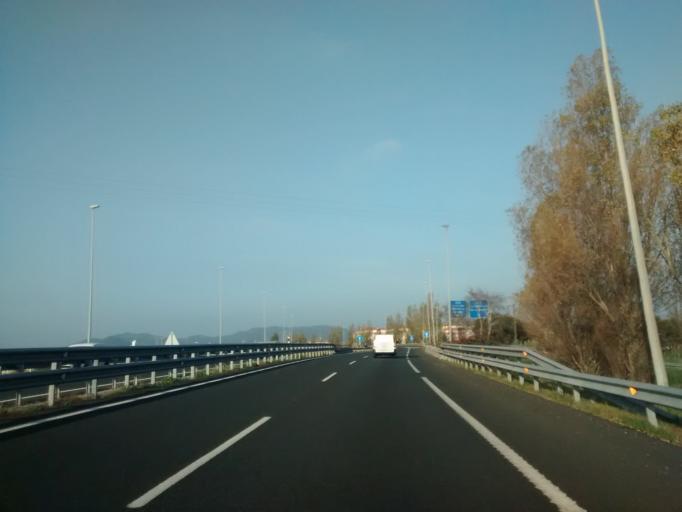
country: ES
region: Cantabria
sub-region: Provincia de Cantabria
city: Santa Cruz de Bezana
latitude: 43.4395
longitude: -3.8885
